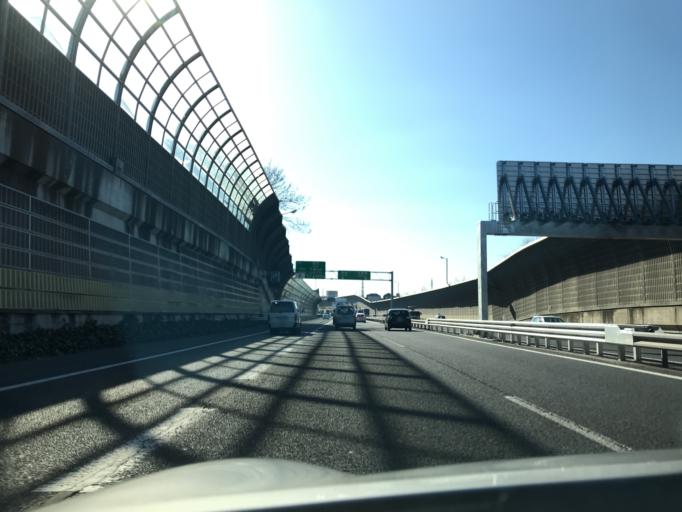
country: JP
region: Chiba
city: Chiba
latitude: 35.6504
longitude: 140.1082
